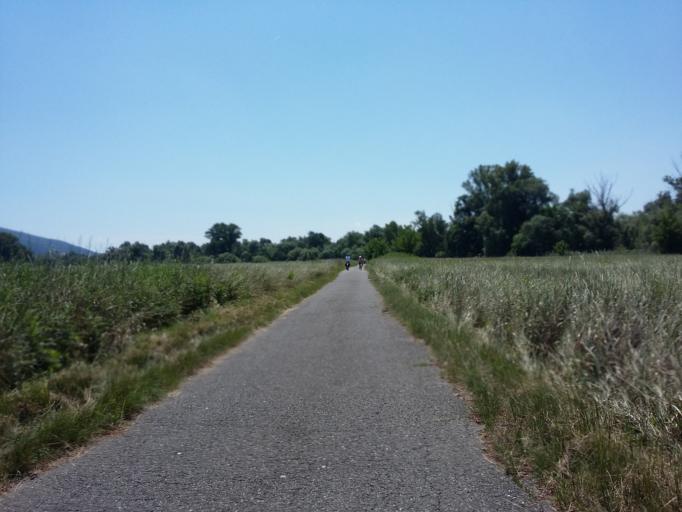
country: AT
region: Lower Austria
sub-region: Politischer Bezirk Ganserndorf
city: Marchegg
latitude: 48.2370
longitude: 16.9484
